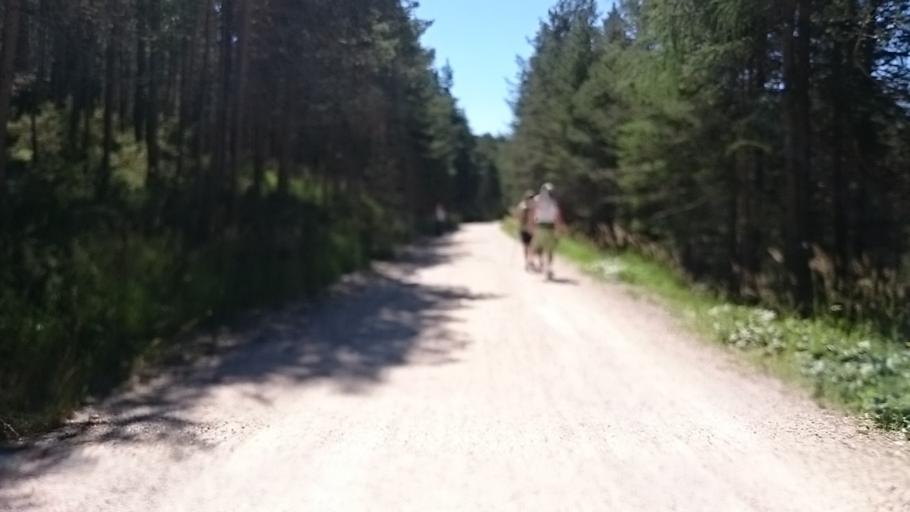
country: IT
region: Veneto
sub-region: Provincia di Belluno
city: Cortina d'Ampezzo
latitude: 46.5704
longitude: 12.1234
